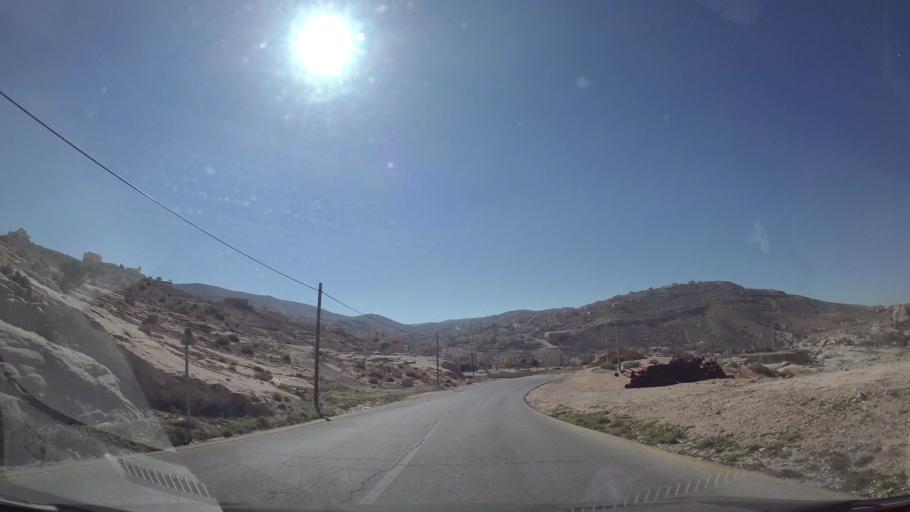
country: JO
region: Ma'an
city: Petra
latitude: 30.3304
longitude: 35.4691
